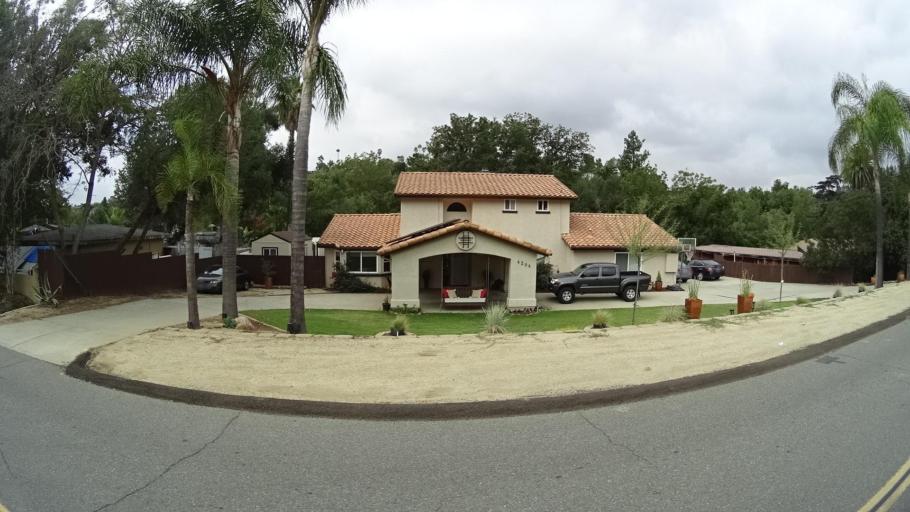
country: US
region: California
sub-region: San Diego County
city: Spring Valley
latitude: 32.7555
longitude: -116.9990
